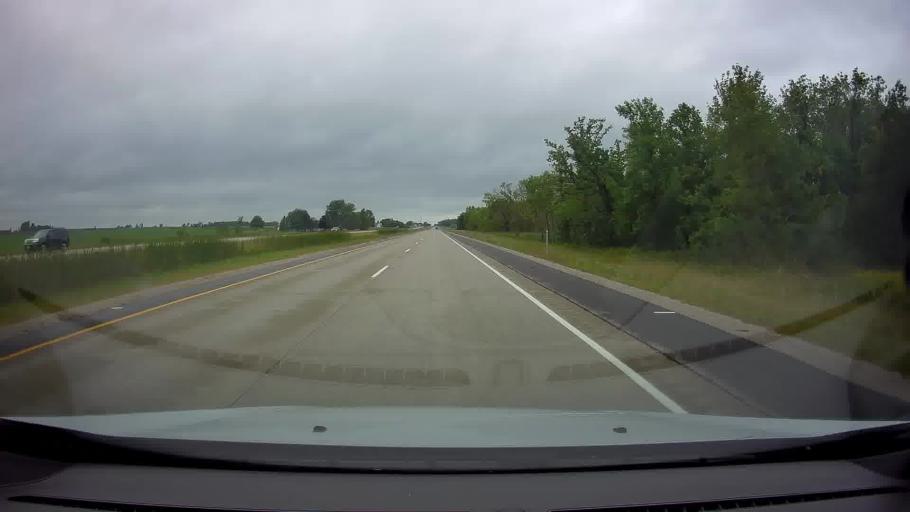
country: US
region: Wisconsin
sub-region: Brown County
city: Pulaski
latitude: 44.6187
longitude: -88.2679
